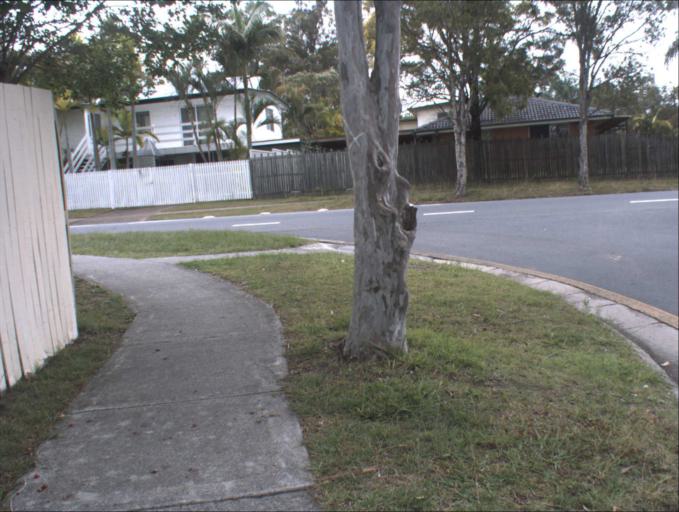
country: AU
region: Queensland
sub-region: Logan
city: Logan City
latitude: -27.6456
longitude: 153.1134
